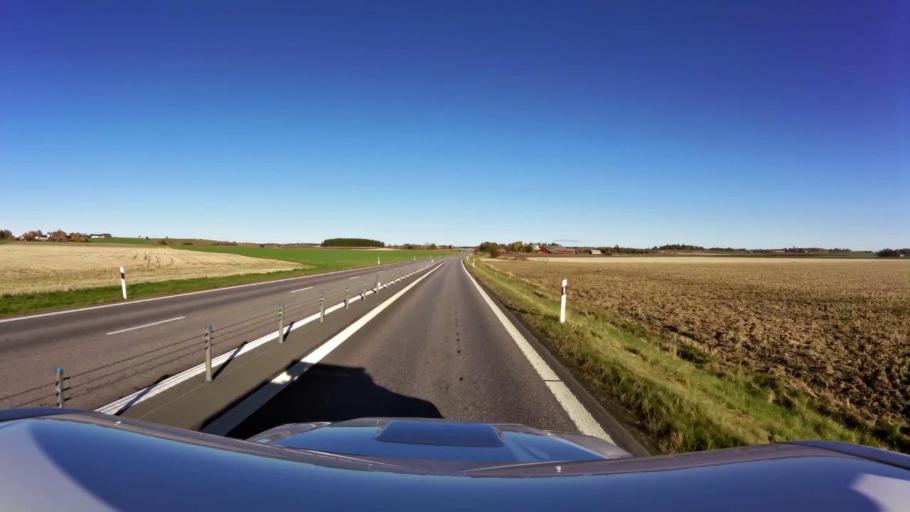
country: SE
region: OEstergoetland
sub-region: Linkopings Kommun
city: Berg
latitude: 58.4608
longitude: 15.4976
